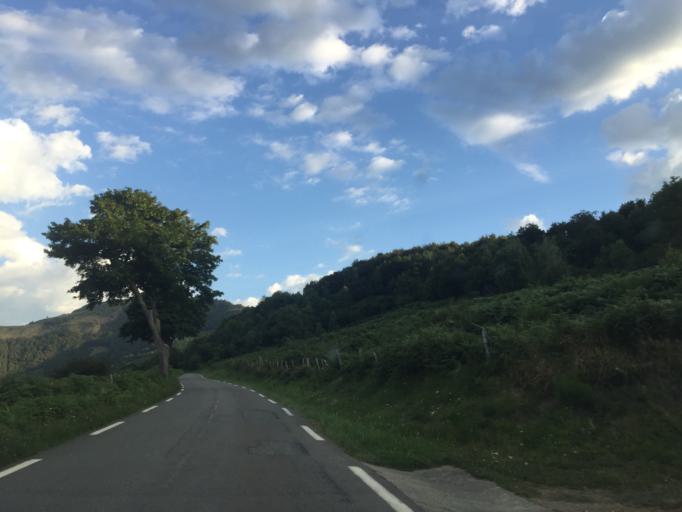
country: FR
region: Midi-Pyrenees
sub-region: Departement des Hautes-Pyrenees
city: Saint-Lary-Soulan
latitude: 42.9286
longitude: 0.3507
